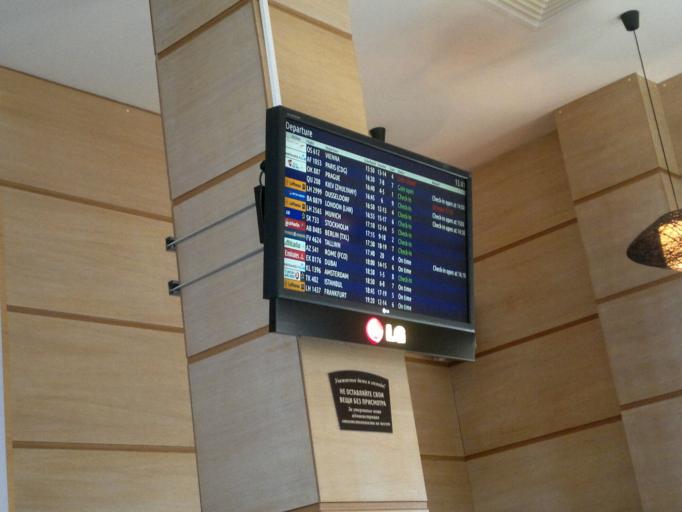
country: RU
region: St.-Petersburg
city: Dachnoye
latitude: 59.8062
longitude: 30.3077
